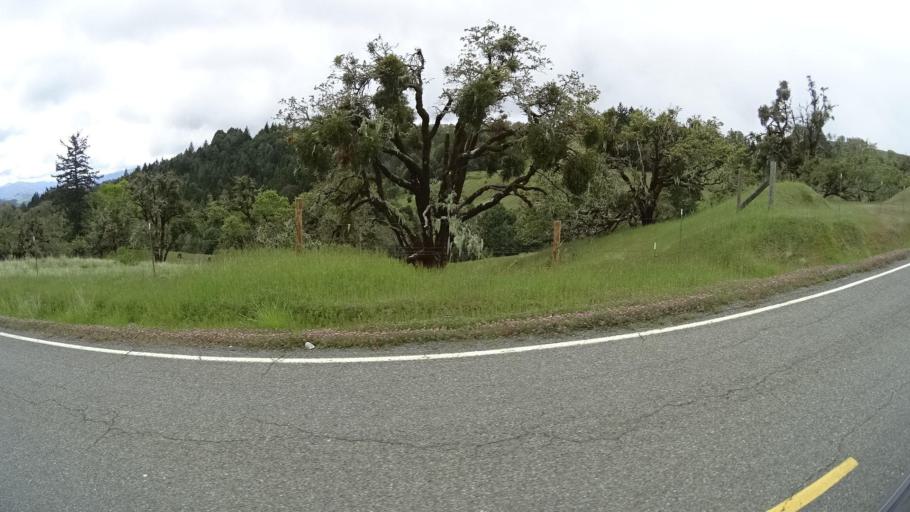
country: US
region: California
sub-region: Humboldt County
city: Redway
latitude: 40.1041
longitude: -123.6801
